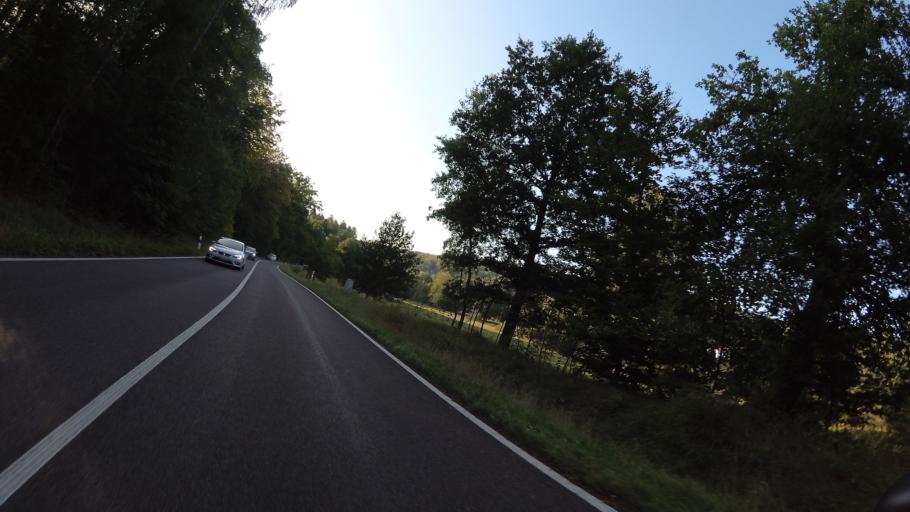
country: DE
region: Saarland
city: Sankt Ingbert
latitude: 49.2513
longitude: 7.1258
